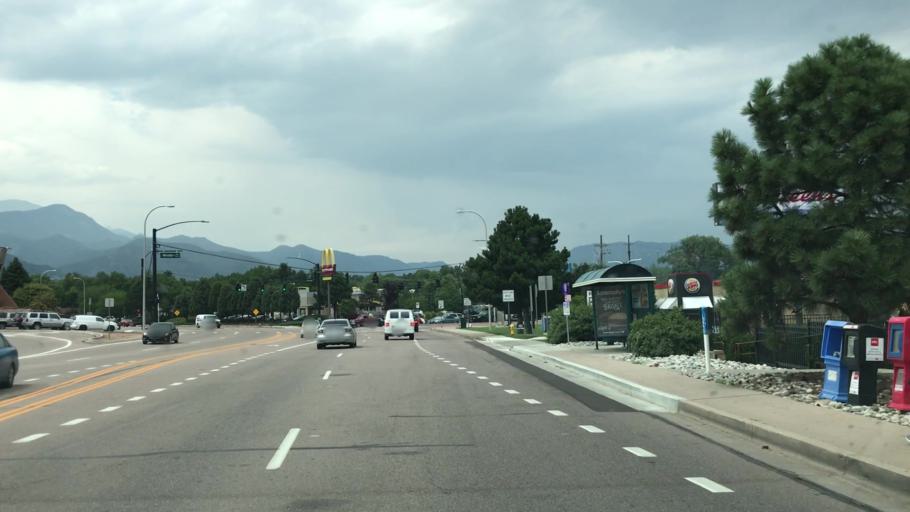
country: US
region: Colorado
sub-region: El Paso County
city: Colorado Springs
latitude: 38.8063
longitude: -104.8211
